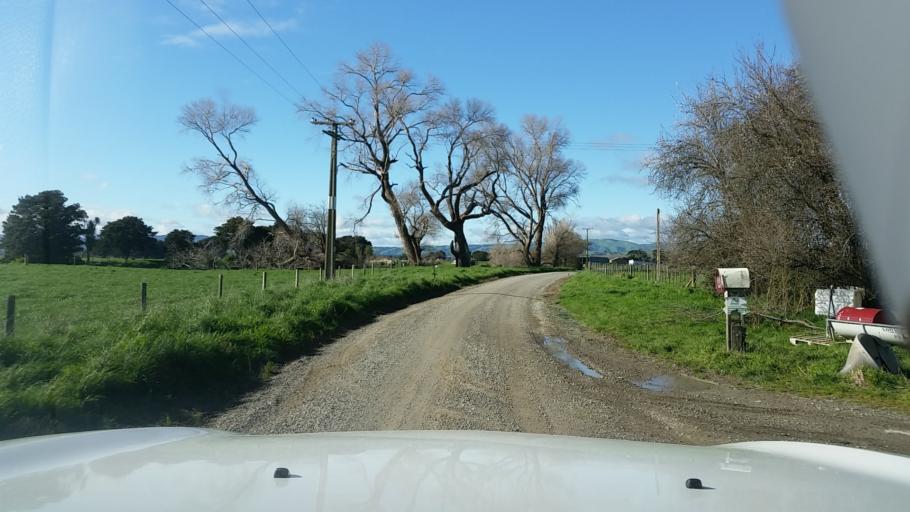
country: NZ
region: Wellington
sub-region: South Wairarapa District
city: Waipawa
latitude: -41.2112
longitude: 175.3942
